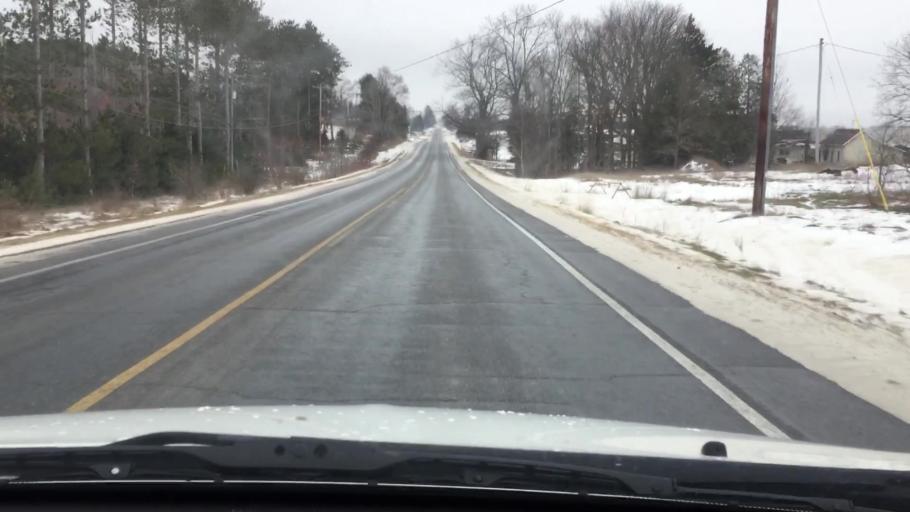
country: US
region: Michigan
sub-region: Wexford County
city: Cadillac
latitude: 44.0768
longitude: -85.4441
